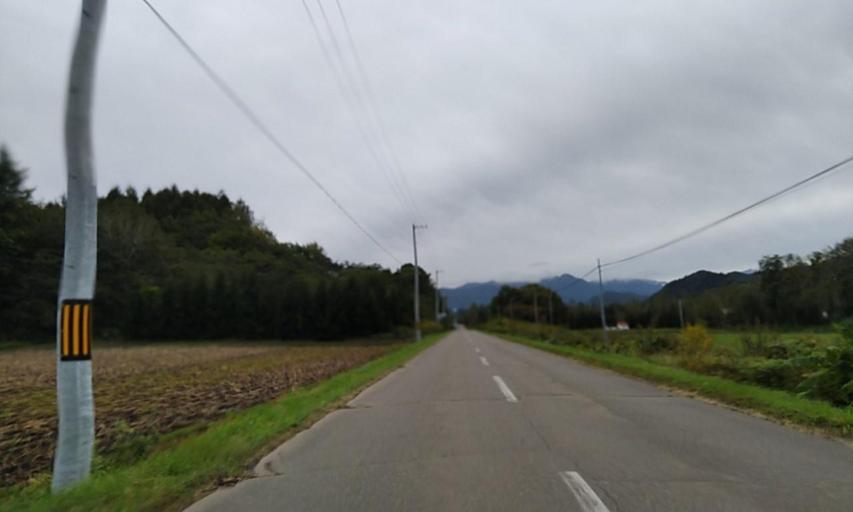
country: JP
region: Hokkaido
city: Obihiro
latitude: 42.6691
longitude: 143.0369
